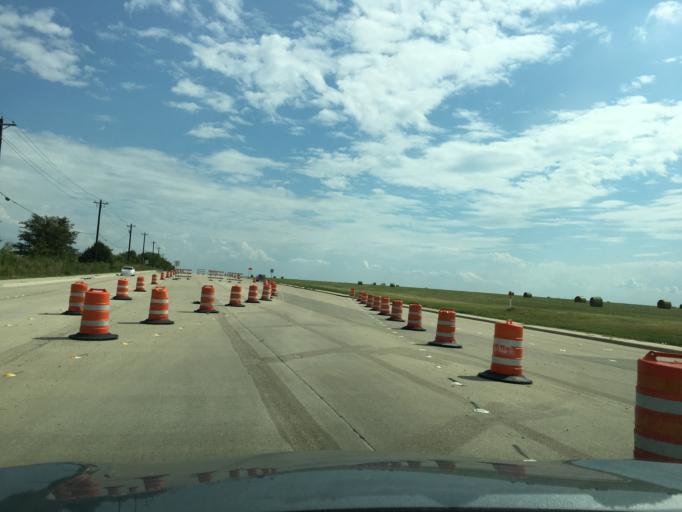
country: US
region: Texas
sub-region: Denton County
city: Oak Point
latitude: 33.1946
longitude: -96.9769
